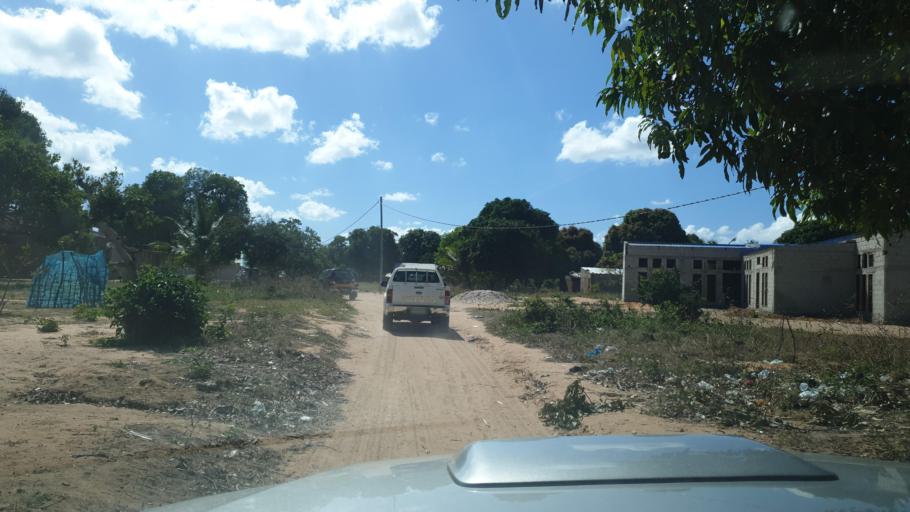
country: MZ
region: Nampula
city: Nacala
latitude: -14.4720
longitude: 40.6928
